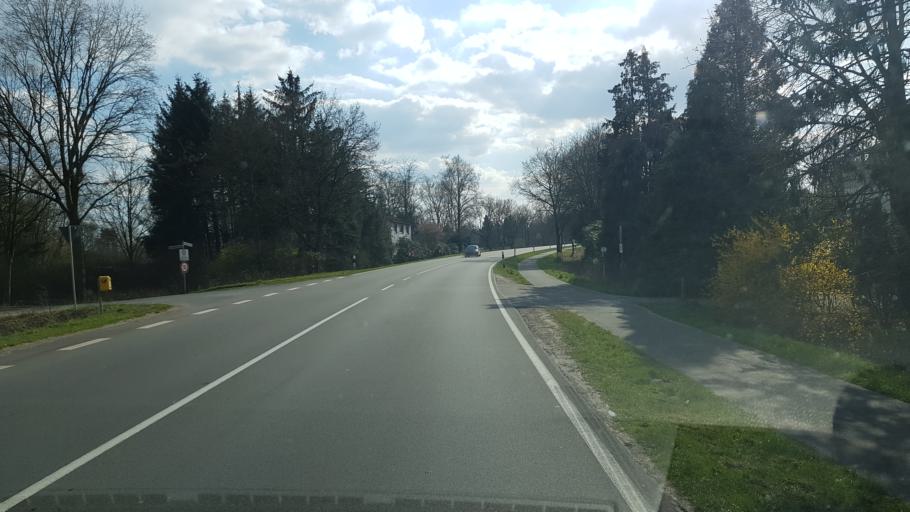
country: DE
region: Lower Saxony
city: Rastede
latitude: 53.2481
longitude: 8.2966
